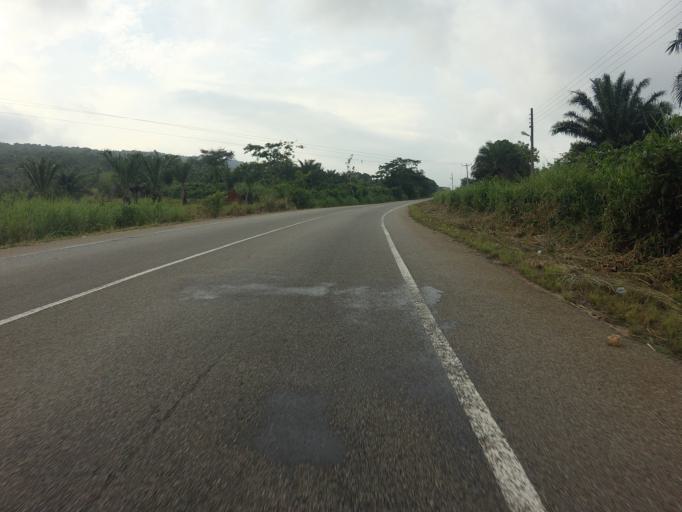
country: GH
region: Volta
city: Ho
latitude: 6.6520
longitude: 0.4695
